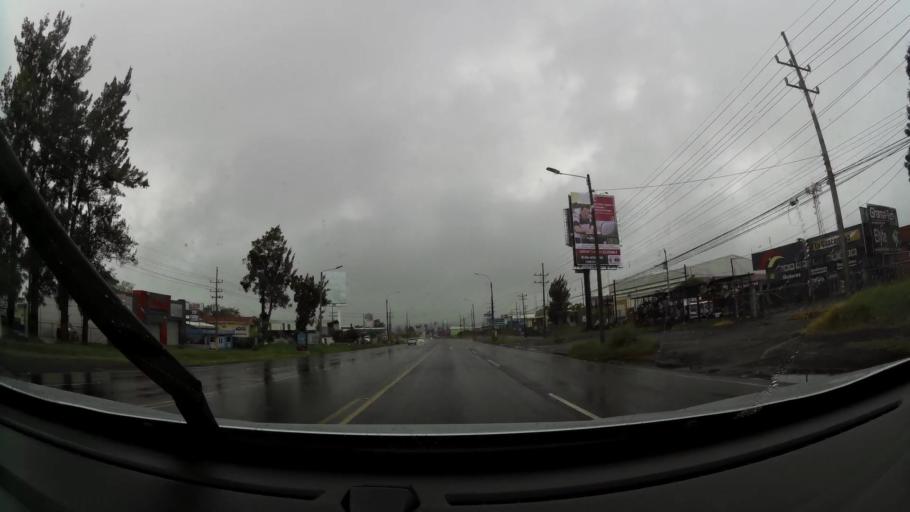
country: CR
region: Cartago
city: Cartago
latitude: 9.8755
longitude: -83.9432
